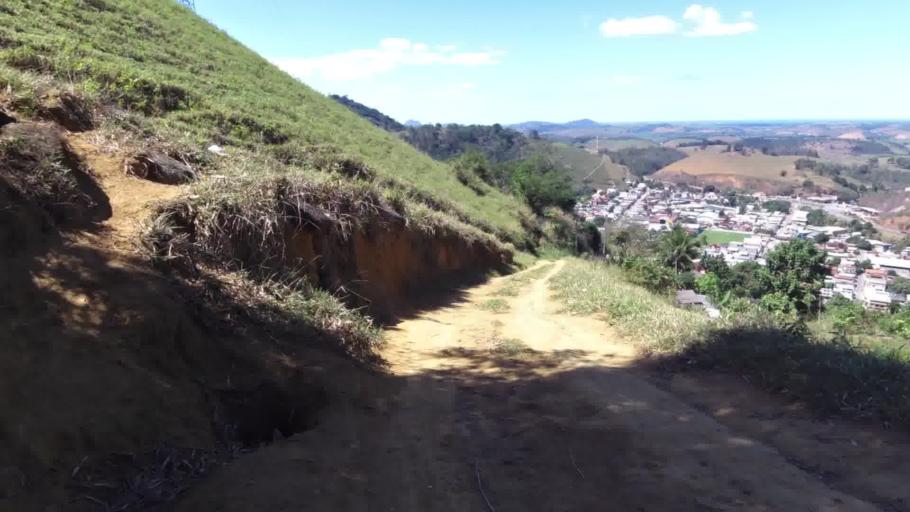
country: BR
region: Espirito Santo
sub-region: Rio Novo Do Sul
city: Rio Novo do Sul
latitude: -20.8598
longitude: -40.9398
